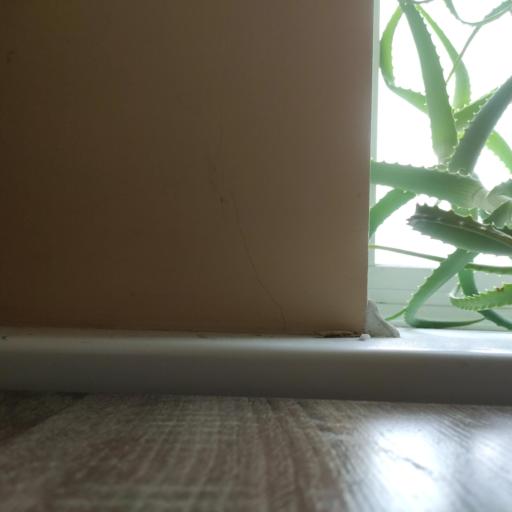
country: RU
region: Moscow
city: Pokrovskoye-Streshnevo
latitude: 55.8034
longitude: 37.4621
